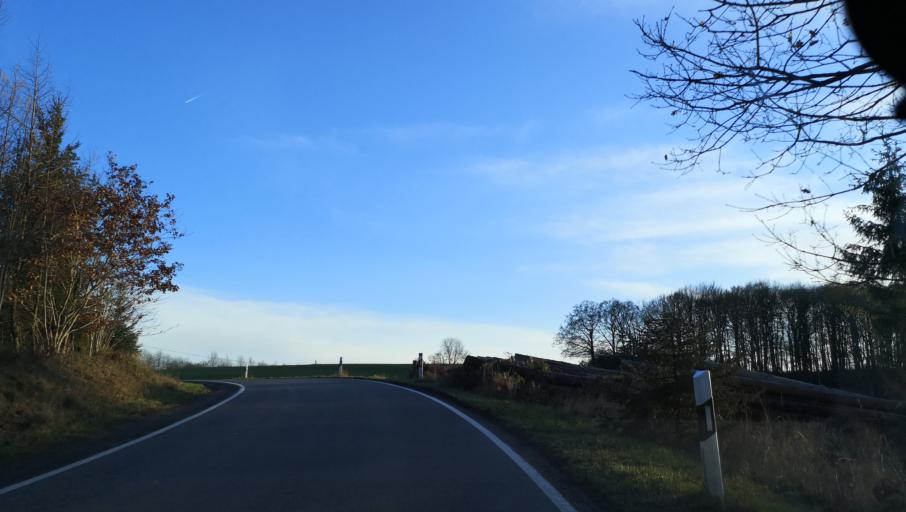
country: DE
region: North Rhine-Westphalia
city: Radevormwald
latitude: 51.1850
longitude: 7.3905
